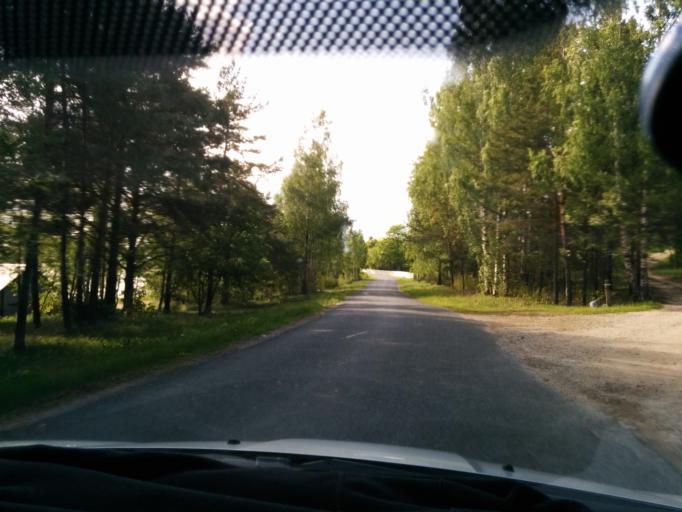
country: EE
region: Harju
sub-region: Loksa linn
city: Loksa
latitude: 59.6094
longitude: 25.7052
